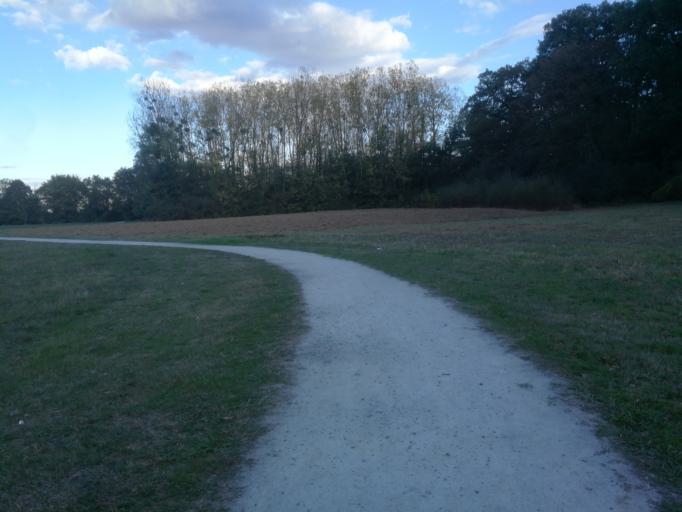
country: FR
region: Centre
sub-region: Departement d'Indre-et-Loire
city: Chanceaux-sur-Choisille
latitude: 47.4388
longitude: 0.6860
